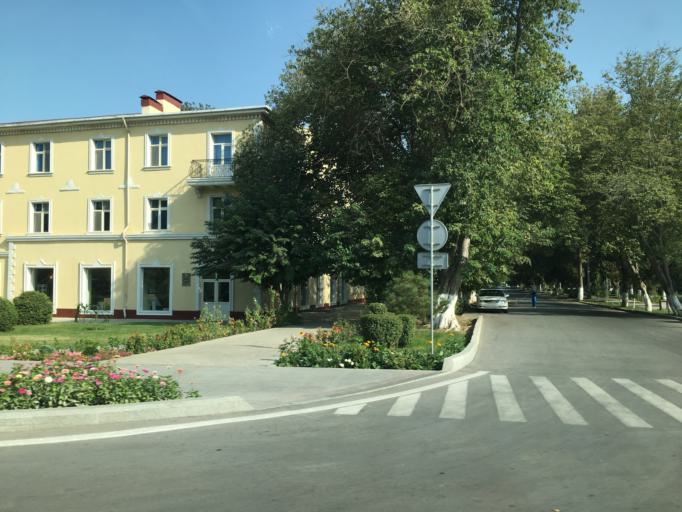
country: TM
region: Ahal
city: Ashgabat
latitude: 37.9344
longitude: 58.3882
